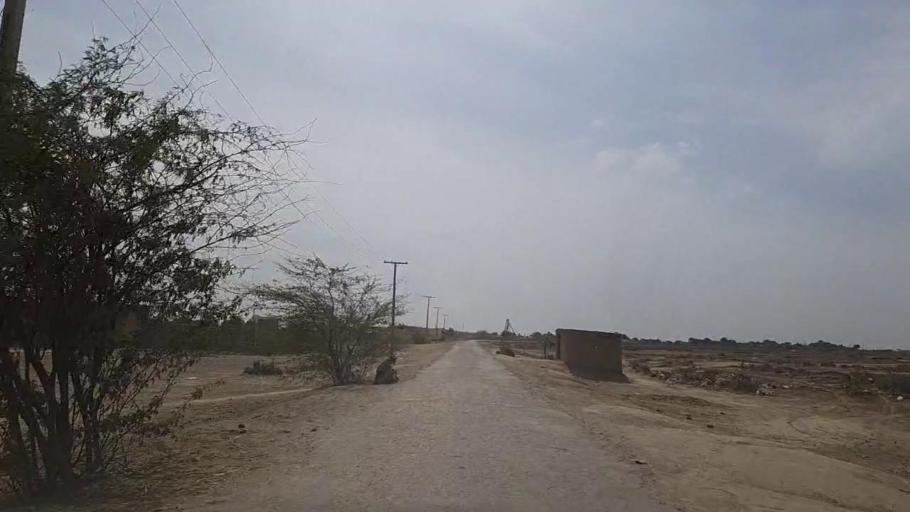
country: PK
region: Sindh
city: Kunri
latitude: 25.2153
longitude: 69.5038
